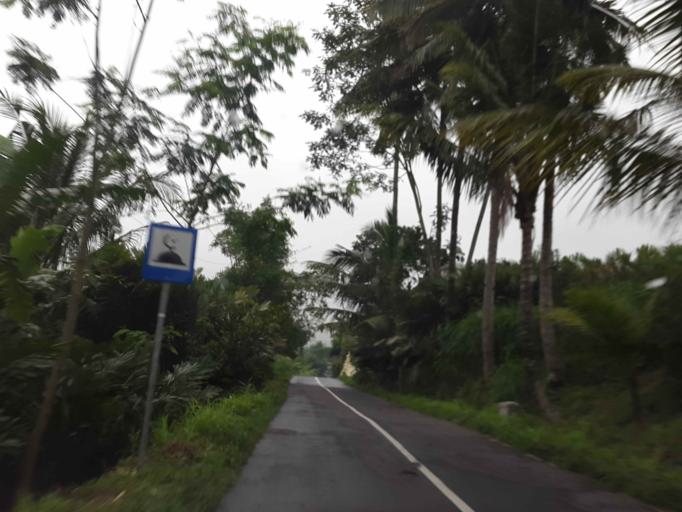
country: ID
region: Central Java
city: Muntilan
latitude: -7.5782
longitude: 110.3480
